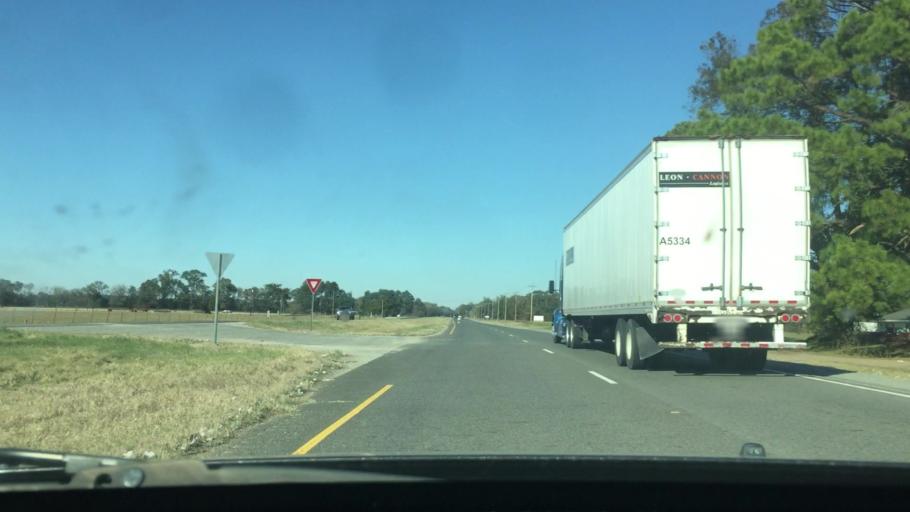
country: US
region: Louisiana
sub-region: Richland Parish
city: Rayville
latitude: 32.3794
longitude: -91.7694
